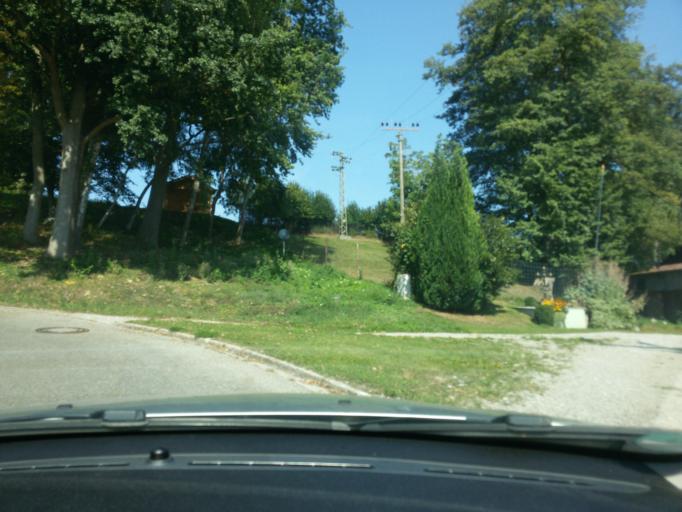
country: DE
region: Bavaria
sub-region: Swabia
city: Munster
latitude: 48.2140
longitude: 10.6135
